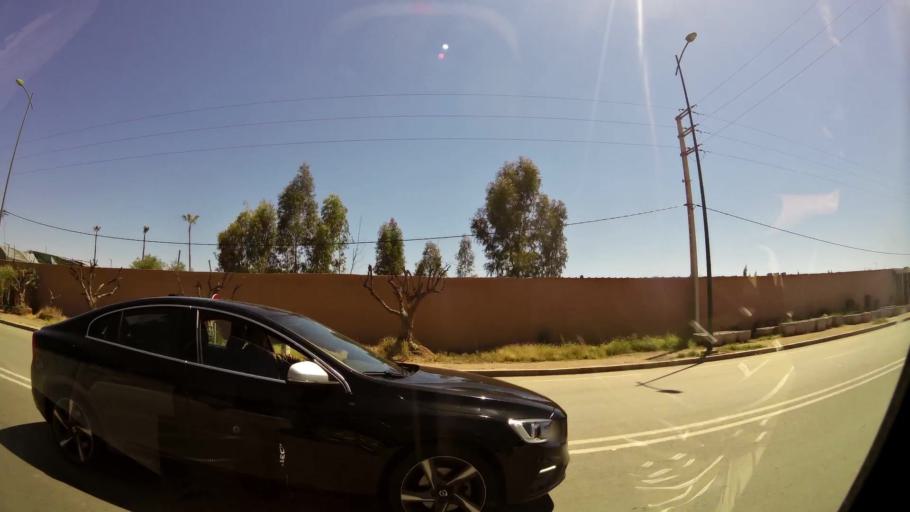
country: MA
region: Marrakech-Tensift-Al Haouz
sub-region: Marrakech
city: Marrakesh
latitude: 31.5740
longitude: -7.9811
